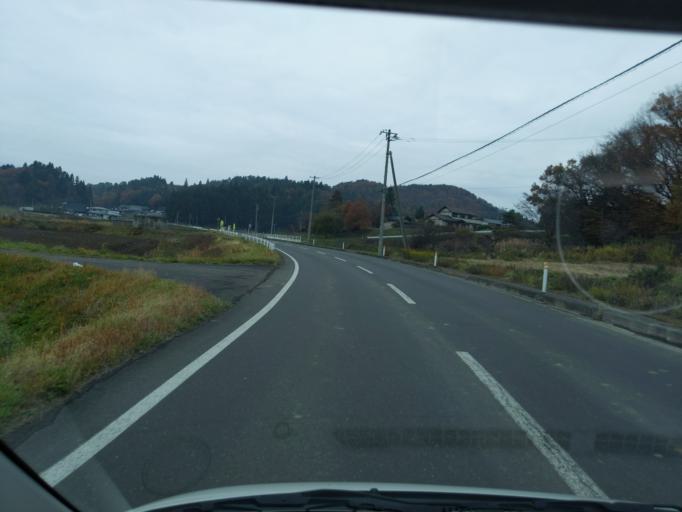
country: JP
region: Iwate
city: Mizusawa
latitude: 39.1769
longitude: 141.2163
